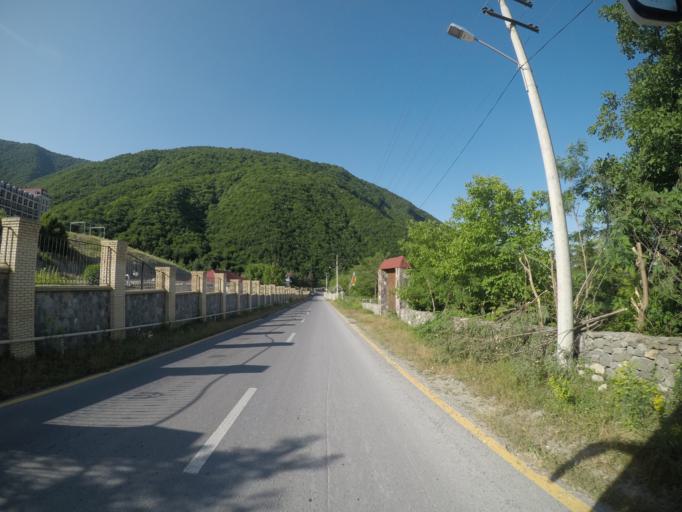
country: AZ
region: Shaki City
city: Sheki
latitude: 41.2462
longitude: 47.2010
